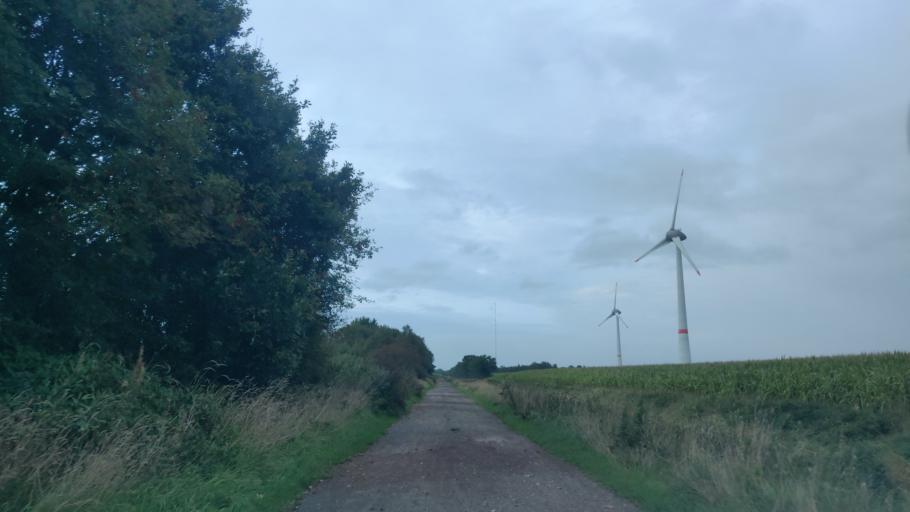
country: DE
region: Lower Saxony
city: Aurich
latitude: 53.4987
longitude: 7.4282
